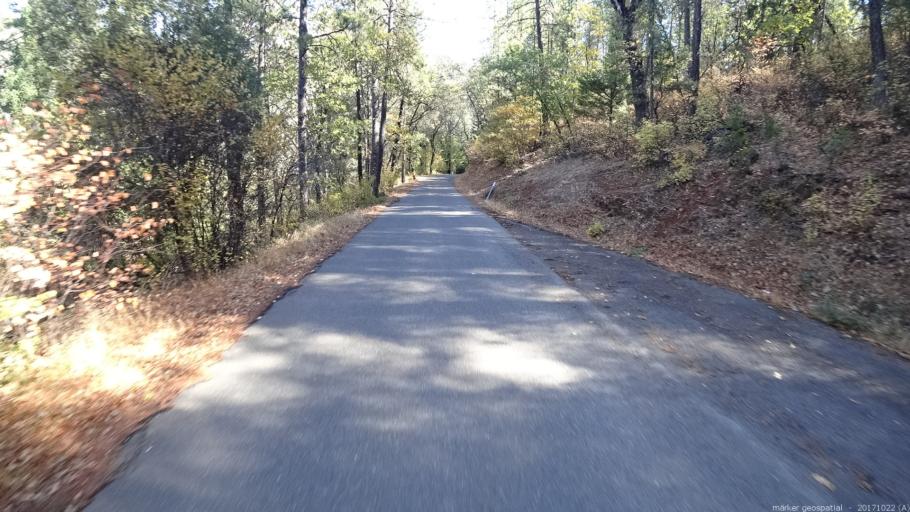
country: US
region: California
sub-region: Shasta County
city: Central Valley (historical)
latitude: 40.9429
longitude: -122.4277
